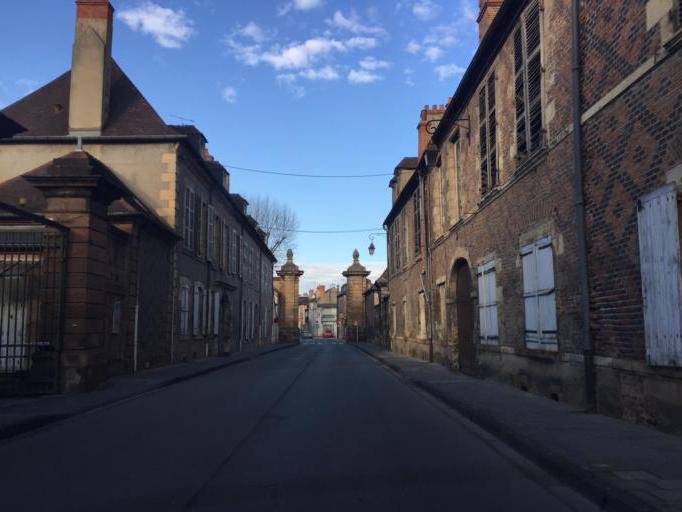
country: FR
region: Auvergne
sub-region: Departement de l'Allier
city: Moulins
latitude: 46.5699
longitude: 3.3294
